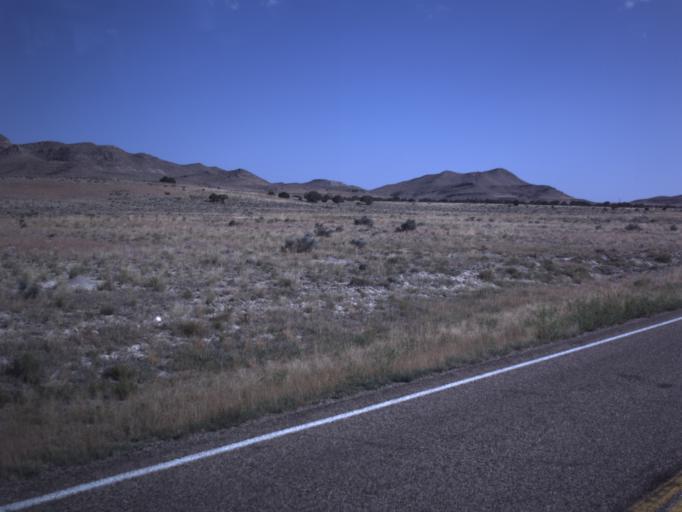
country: US
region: Utah
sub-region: Beaver County
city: Milford
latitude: 38.8285
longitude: -112.8499
